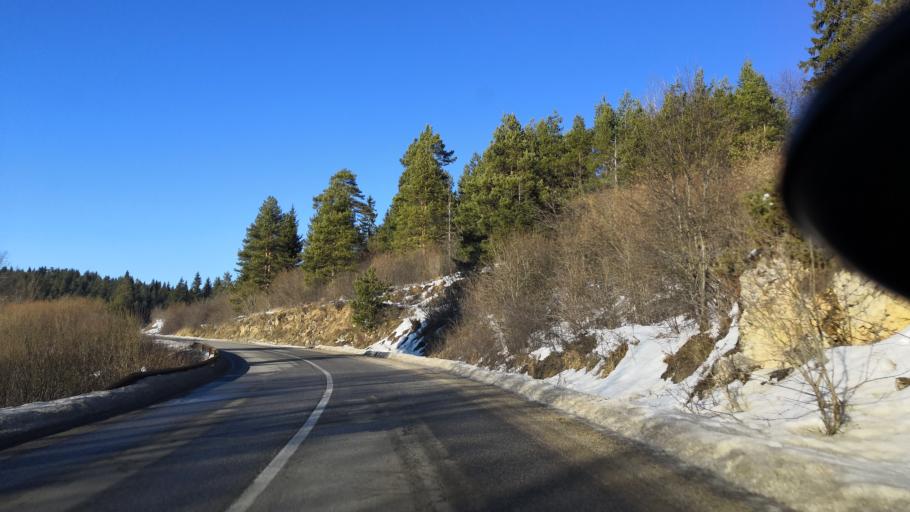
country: BA
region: Republika Srpska
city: Han Pijesak
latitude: 44.0196
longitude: 18.8834
